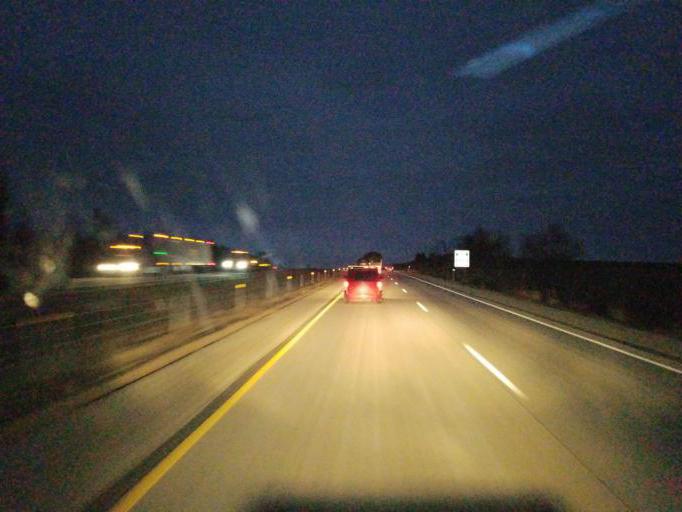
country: US
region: Iowa
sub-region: Guthrie County
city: Guthrie Center
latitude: 41.4931
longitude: -94.6025
